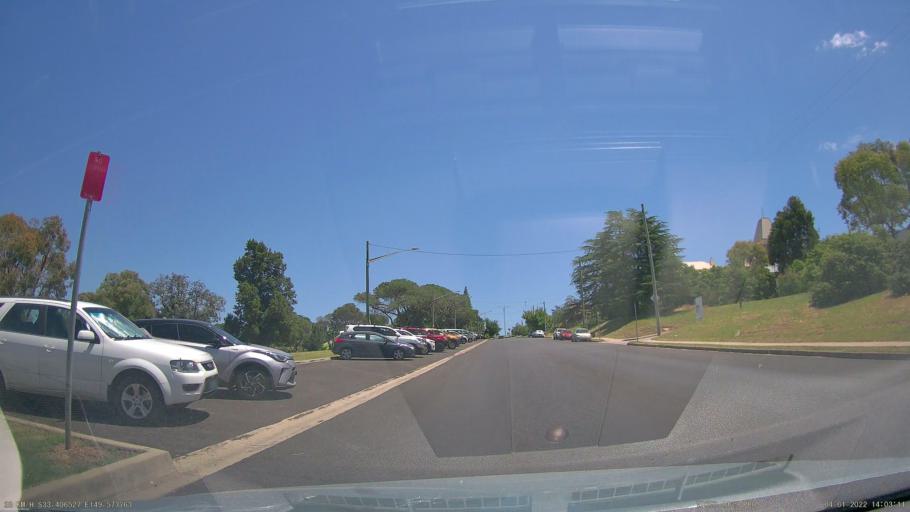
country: AU
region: New South Wales
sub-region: Bathurst Regional
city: Bathurst
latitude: -33.4066
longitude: 149.5737
